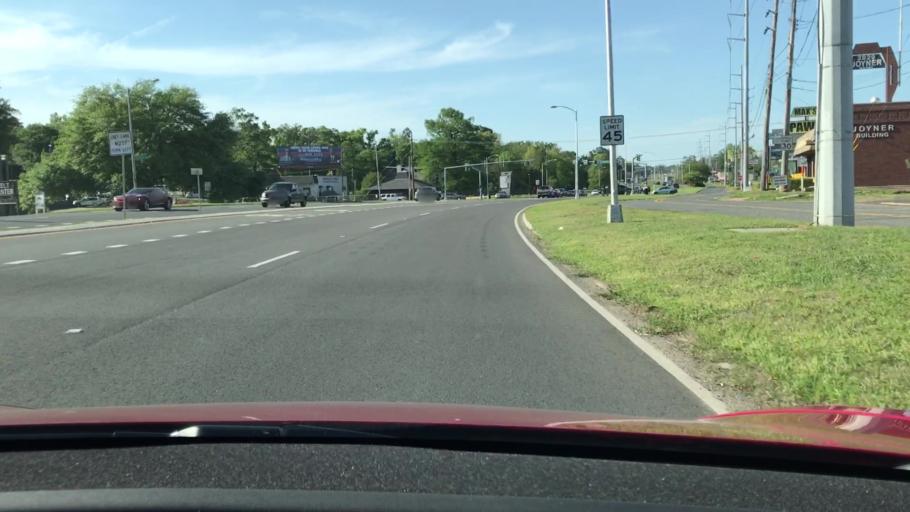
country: US
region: Louisiana
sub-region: Bossier Parish
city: Bossier City
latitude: 32.4835
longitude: -93.7238
